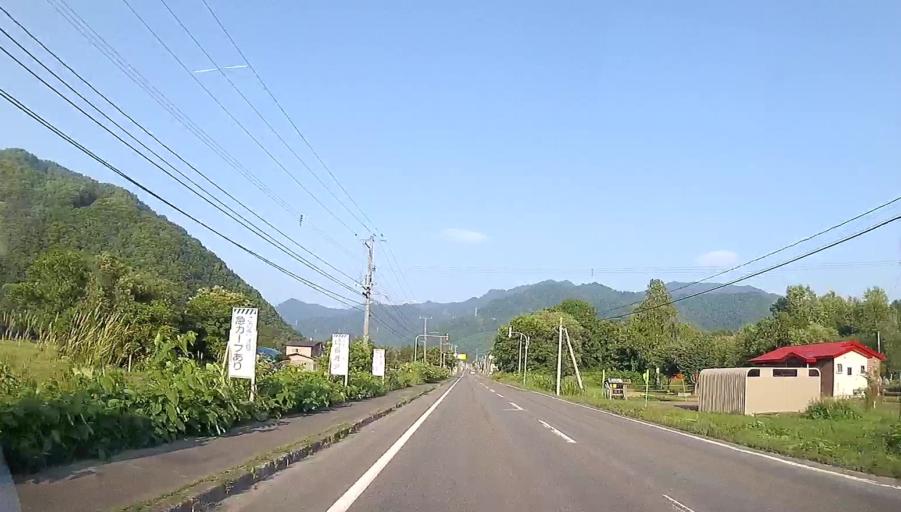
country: JP
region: Hokkaido
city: Shimo-furano
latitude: 42.8927
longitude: 142.5270
